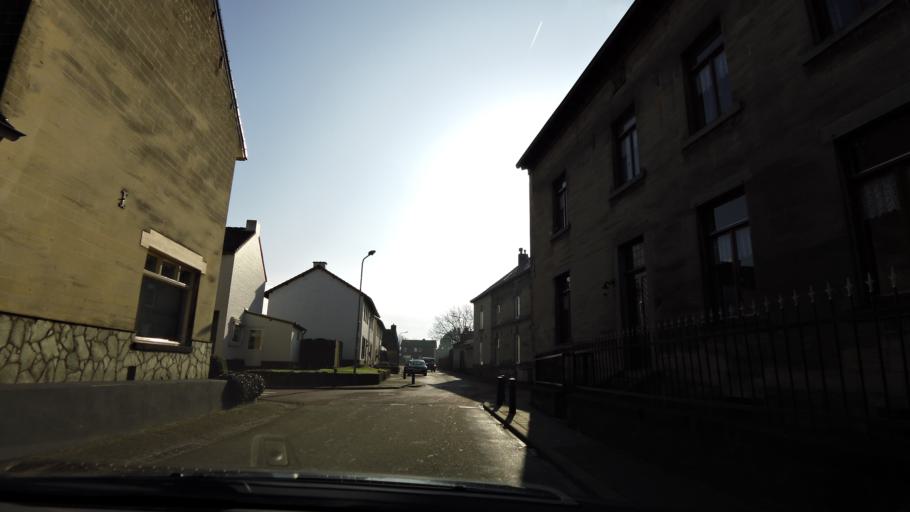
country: NL
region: Limburg
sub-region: Valkenburg aan de Geul
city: Sibbe
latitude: 50.8392
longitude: 5.8316
